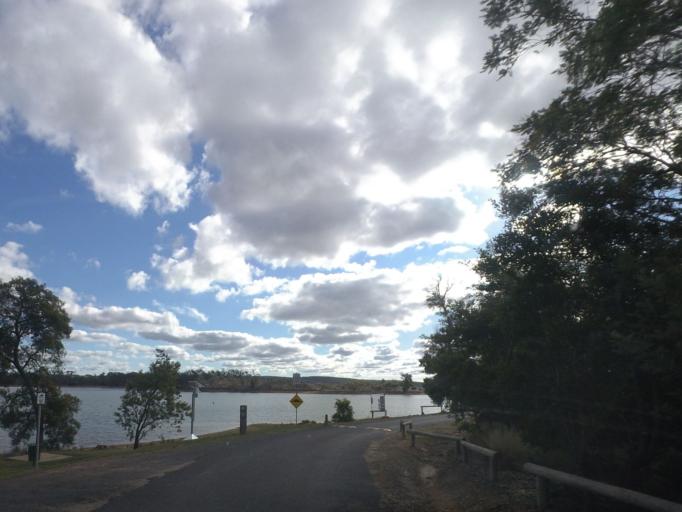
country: AU
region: Victoria
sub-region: Mount Alexander
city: Castlemaine
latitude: -37.2558
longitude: 144.3817
